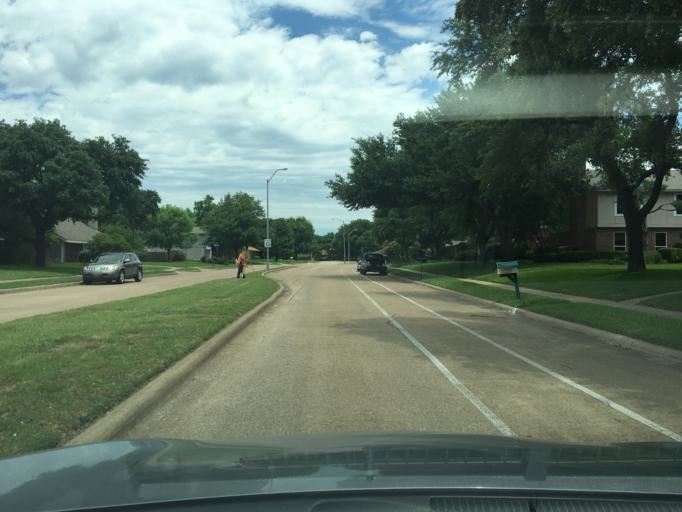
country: US
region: Texas
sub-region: Dallas County
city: Richardson
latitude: 32.9623
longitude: -96.6916
